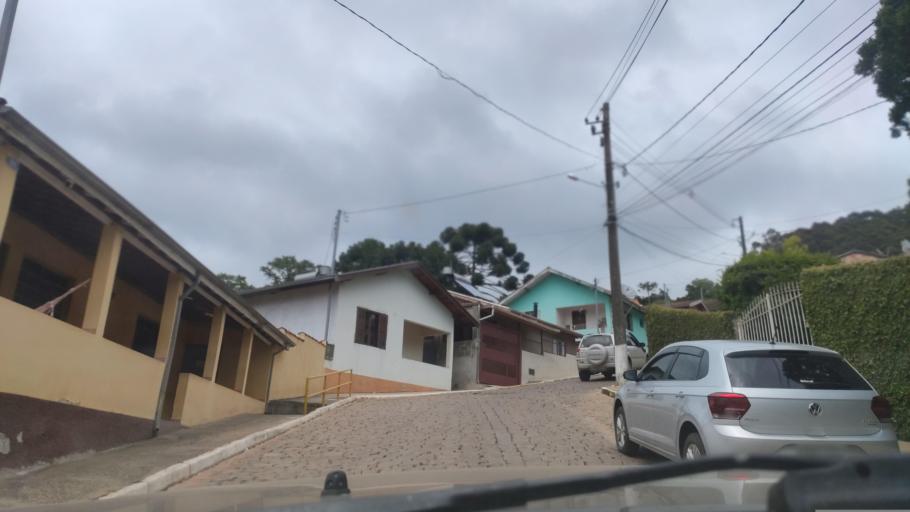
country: BR
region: Minas Gerais
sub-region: Paraisopolis
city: Paraisopolis
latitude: -22.6593
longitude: -45.8575
